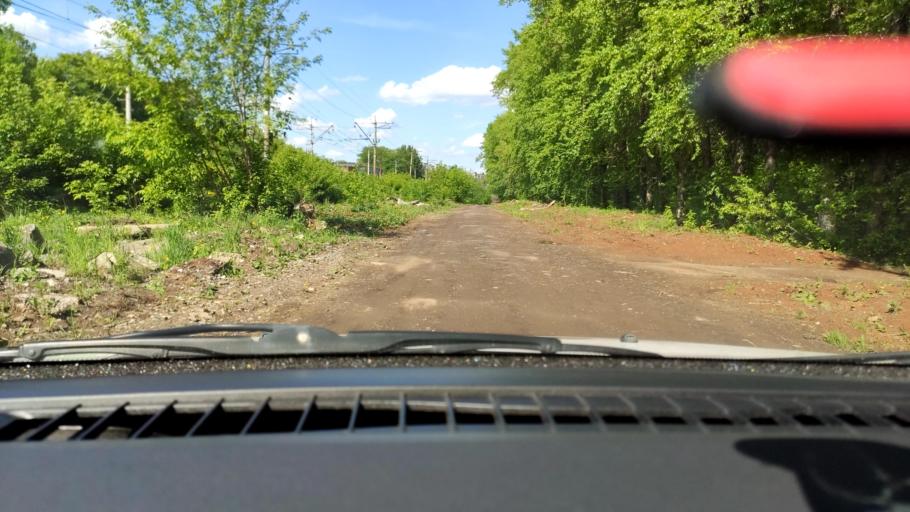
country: RU
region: Perm
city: Perm
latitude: 57.9656
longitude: 56.2067
